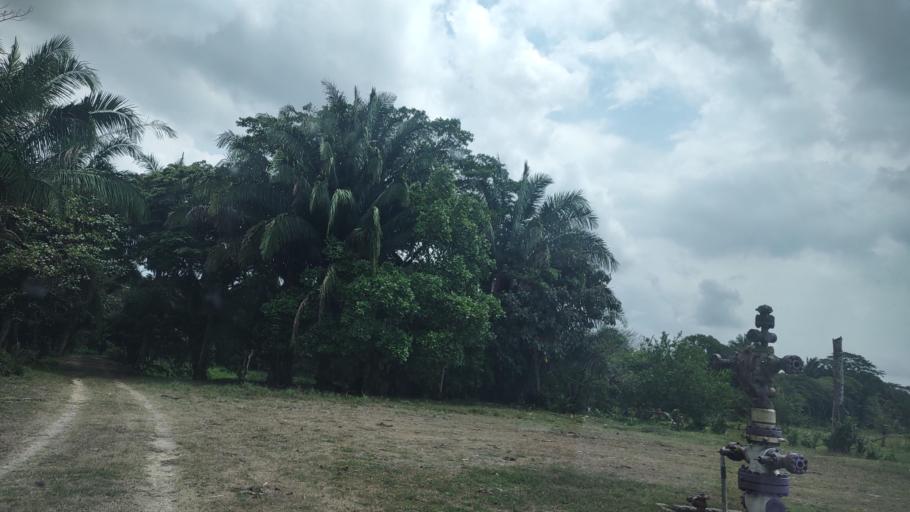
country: MX
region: Veracruz
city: Las Choapas
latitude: 17.9674
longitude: -94.1256
